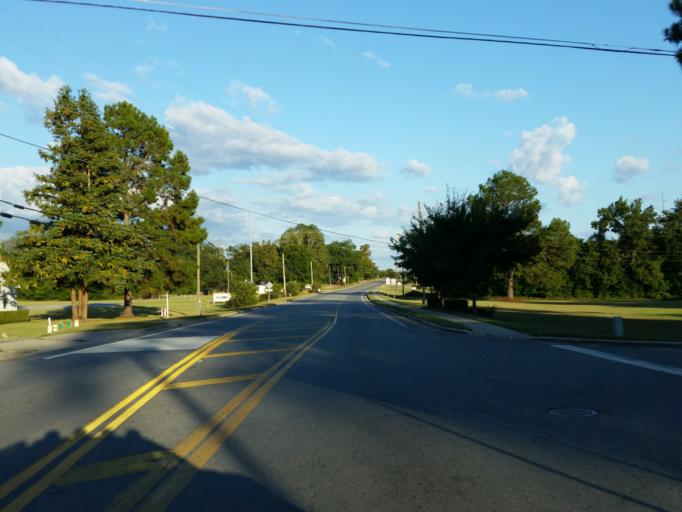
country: US
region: Georgia
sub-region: Dooly County
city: Vienna
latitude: 32.0901
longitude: -83.7820
